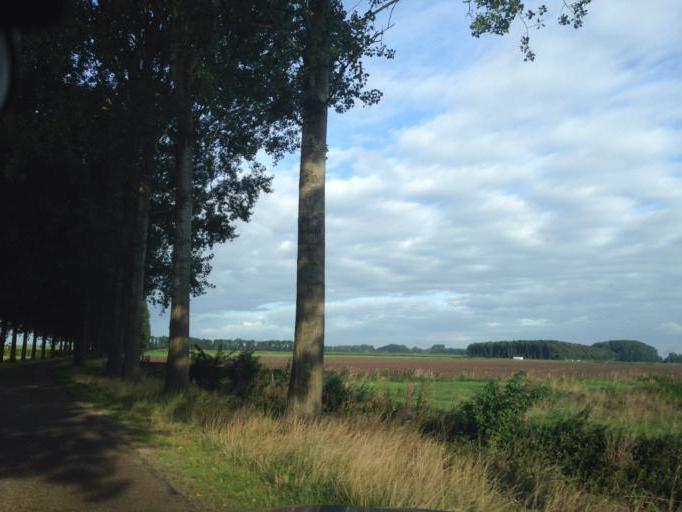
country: NL
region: South Holland
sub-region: Gemeente Leerdam
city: Leerdam
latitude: 51.8612
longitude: 5.1507
